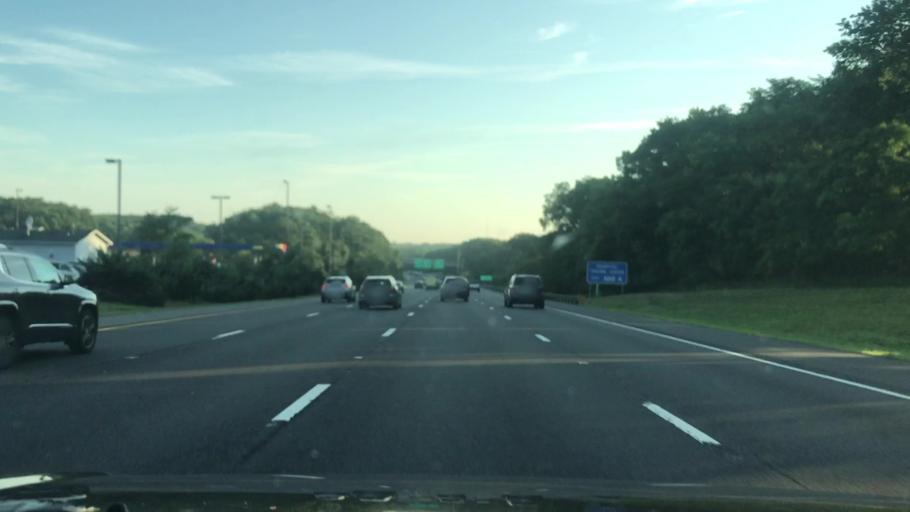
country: US
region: New Jersey
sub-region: Monmouth County
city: Shark River Hills
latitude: 40.1990
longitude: -74.0983
